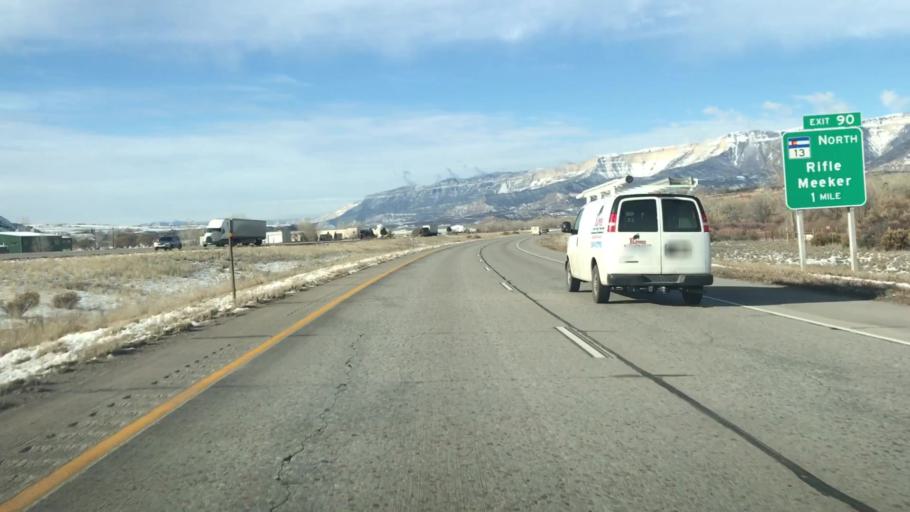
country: US
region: Colorado
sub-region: Garfield County
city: Rifle
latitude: 39.5252
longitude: -107.7557
